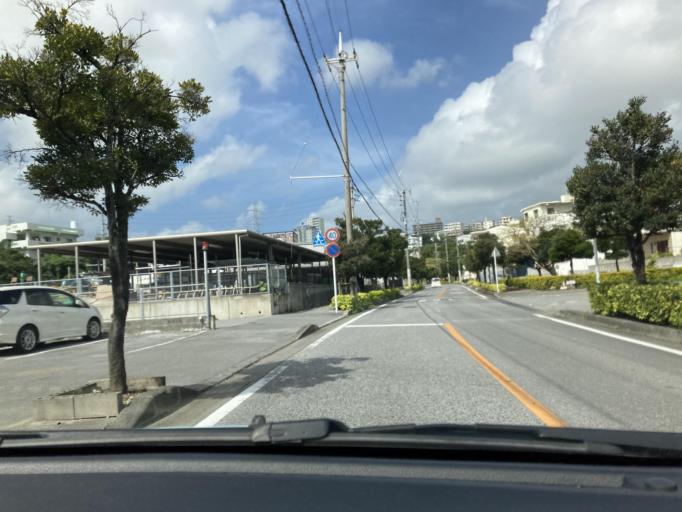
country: JP
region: Okinawa
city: Okinawa
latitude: 26.3207
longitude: 127.8166
